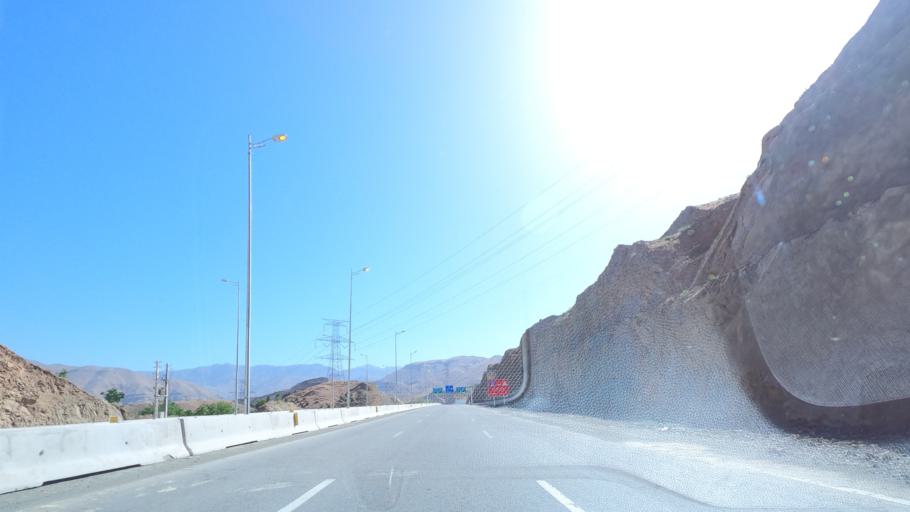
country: IR
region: Alborz
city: Karaj
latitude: 35.8128
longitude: 51.0365
